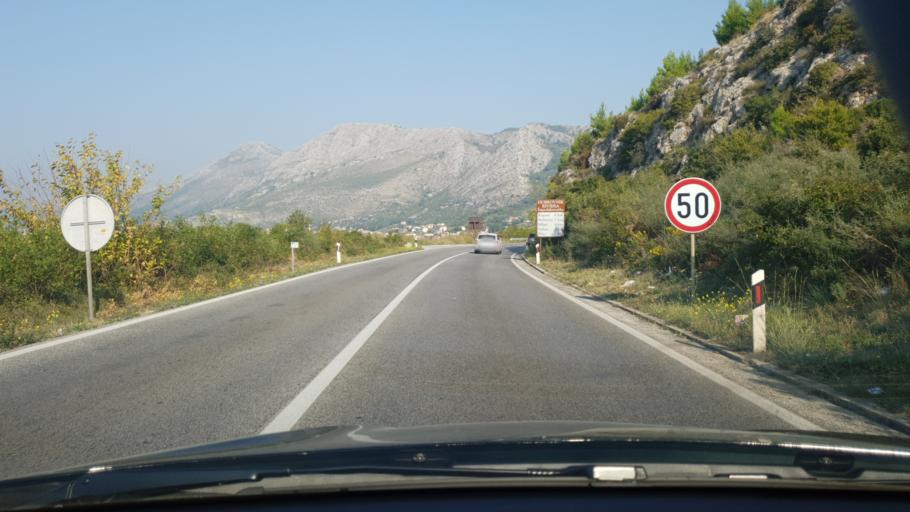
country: HR
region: Dubrovacko-Neretvanska
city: Cavtat
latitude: 42.5967
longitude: 18.2310
